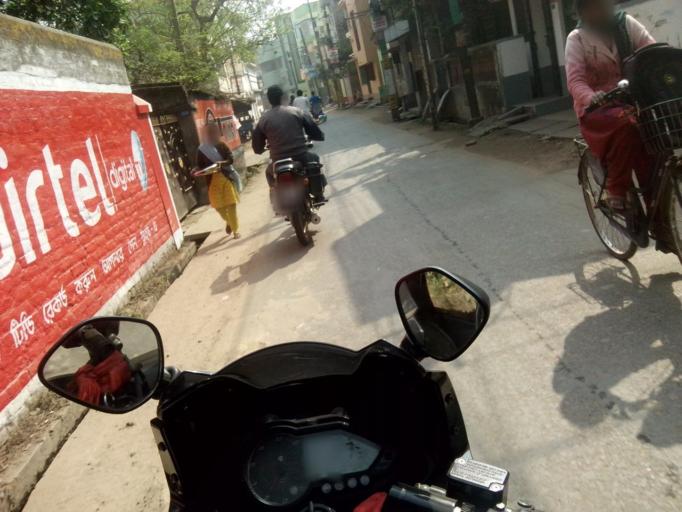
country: IN
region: West Bengal
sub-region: Barddhaman
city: Barddhaman
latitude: 23.2404
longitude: 87.8619
